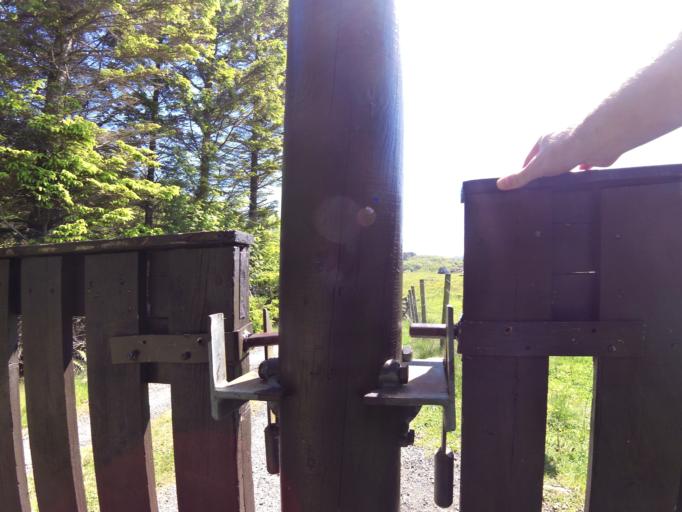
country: NO
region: Rogaland
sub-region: Eigersund
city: Egersund
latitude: 58.5029
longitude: 5.8996
